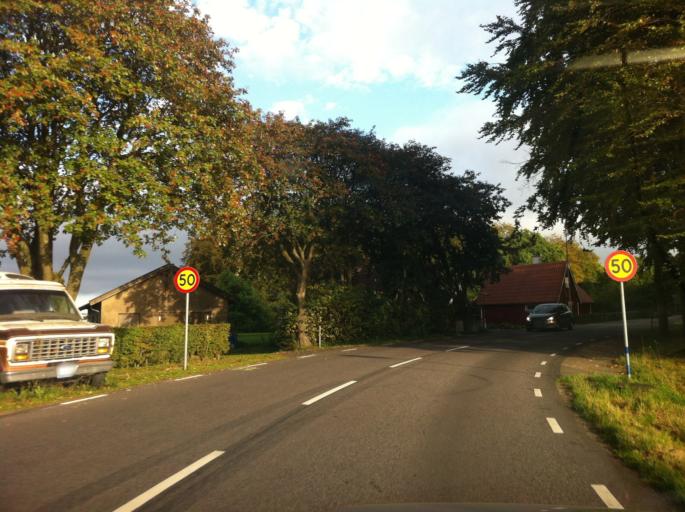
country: SE
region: Skane
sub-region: Helsingborg
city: Hyllinge
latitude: 56.0708
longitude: 12.7985
